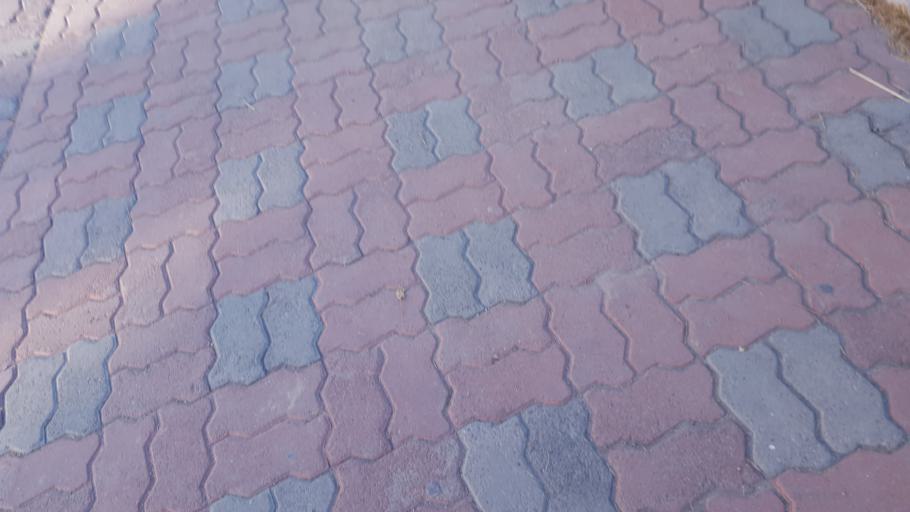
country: MN
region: Ulaanbaatar
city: Ulaanbaatar
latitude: 47.8808
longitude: 106.9131
